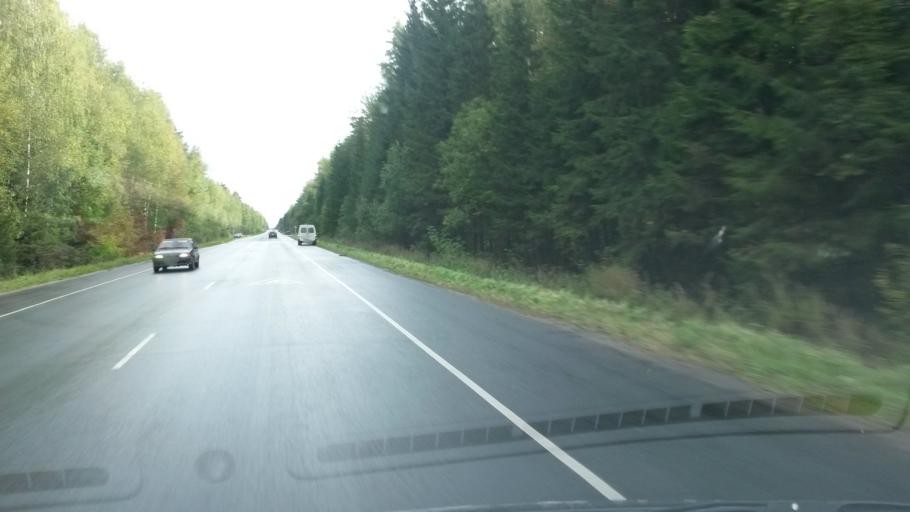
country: RU
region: Ivanovo
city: Kitovo
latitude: 57.0373
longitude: 41.3269
